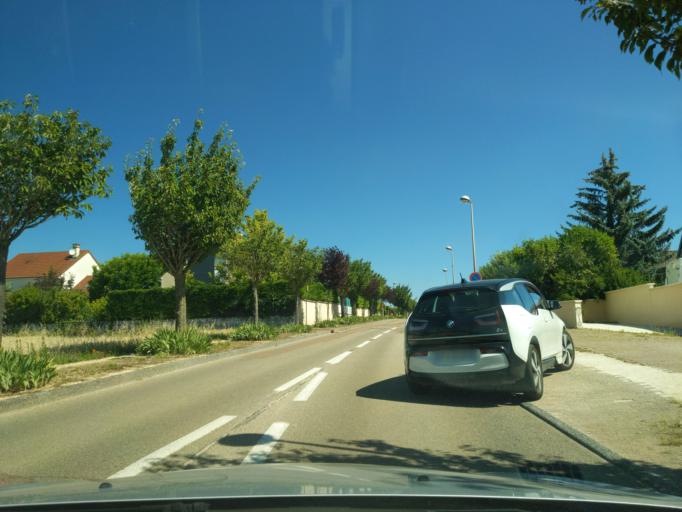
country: FR
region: Bourgogne
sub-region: Departement de la Cote-d'Or
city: Ruffey-les-Echirey
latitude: 47.3765
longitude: 5.0689
